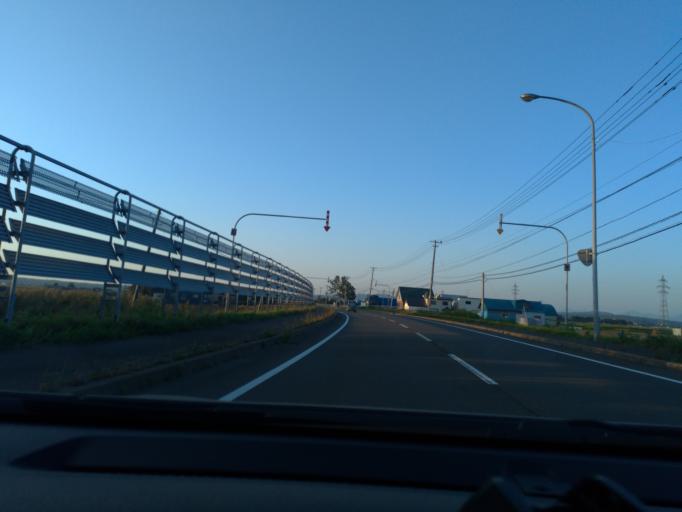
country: JP
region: Hokkaido
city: Tobetsu
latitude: 43.1909
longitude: 141.5244
